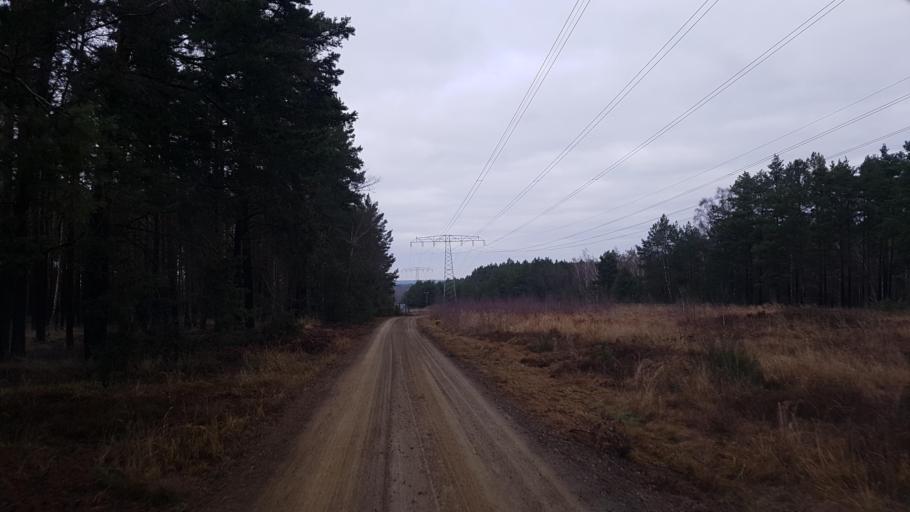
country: DE
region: Brandenburg
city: Altdobern
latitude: 51.6430
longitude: 14.0048
